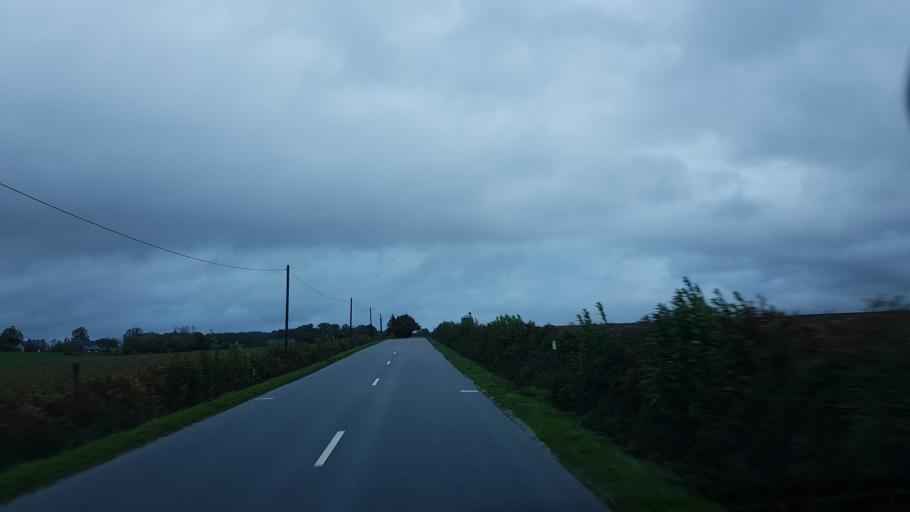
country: FR
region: Brittany
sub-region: Departement d'Ille-et-Vilaine
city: Balaze
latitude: 48.1455
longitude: -1.1634
